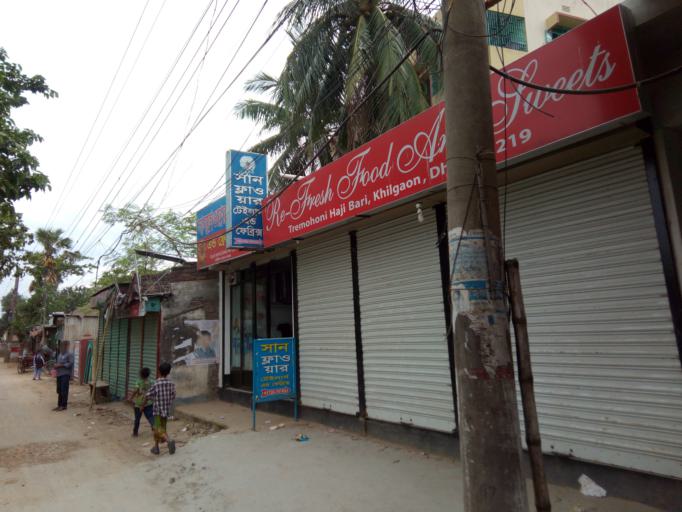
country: BD
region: Dhaka
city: Paltan
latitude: 23.7554
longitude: 90.4556
